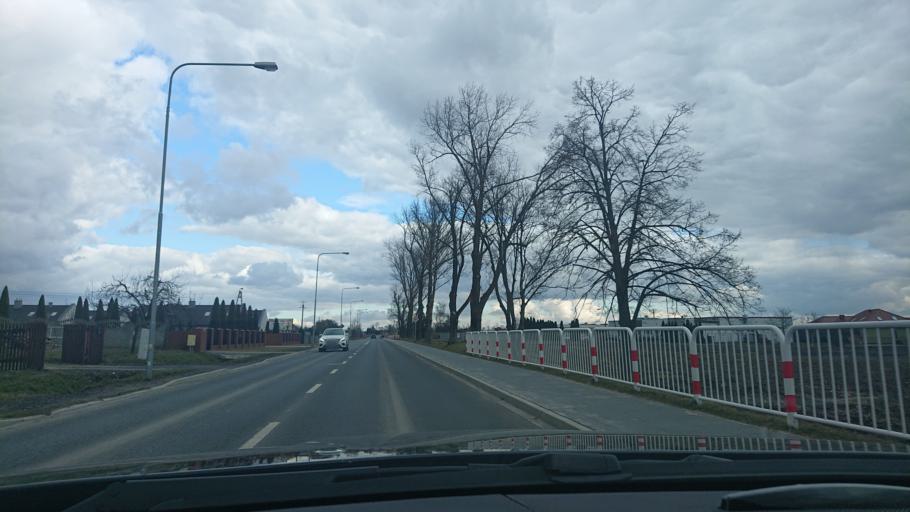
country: PL
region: Greater Poland Voivodeship
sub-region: Powiat gnieznienski
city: Gniezno
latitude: 52.5421
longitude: 17.6521
